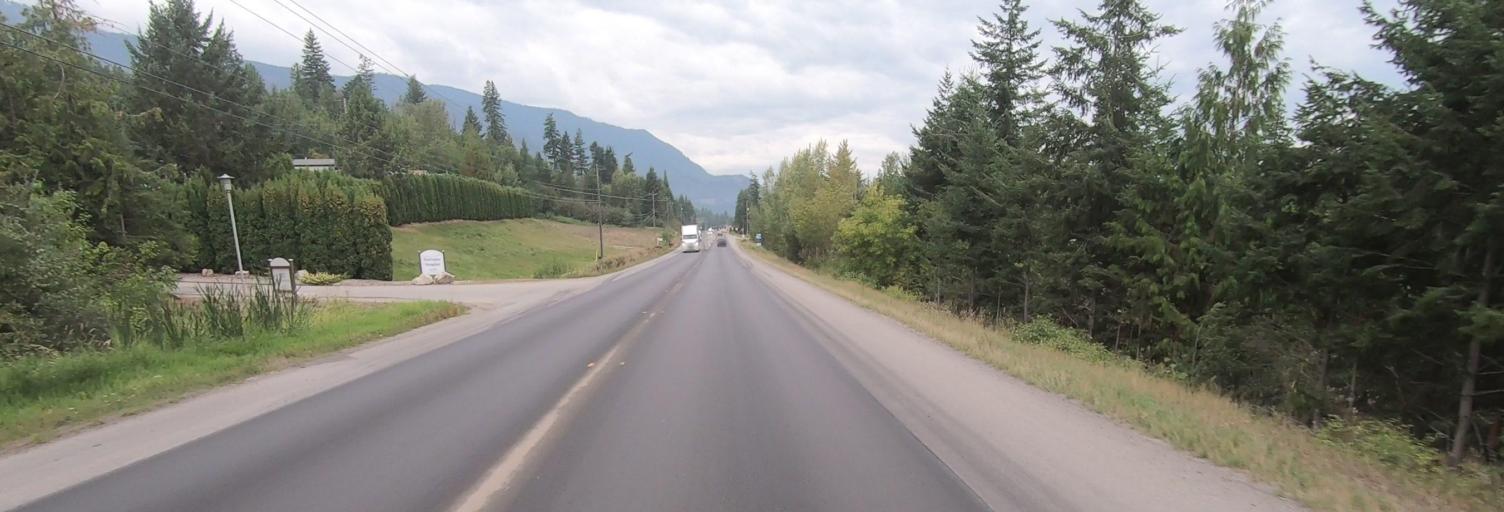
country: CA
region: British Columbia
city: Salmon Arm
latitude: 50.8770
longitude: -119.4547
